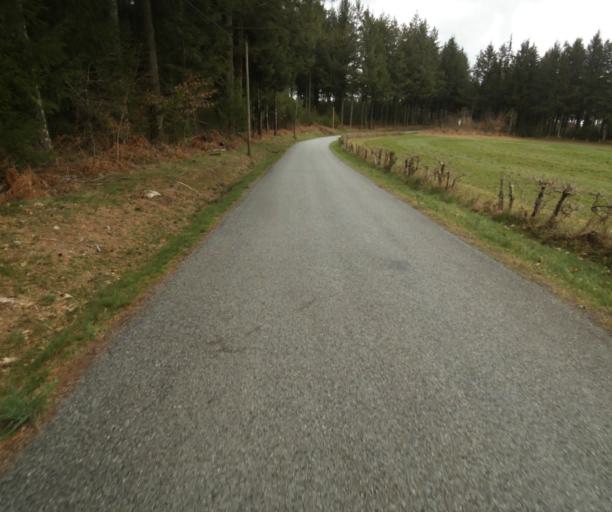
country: FR
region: Limousin
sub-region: Departement de la Correze
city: Correze
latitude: 45.3229
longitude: 1.9176
